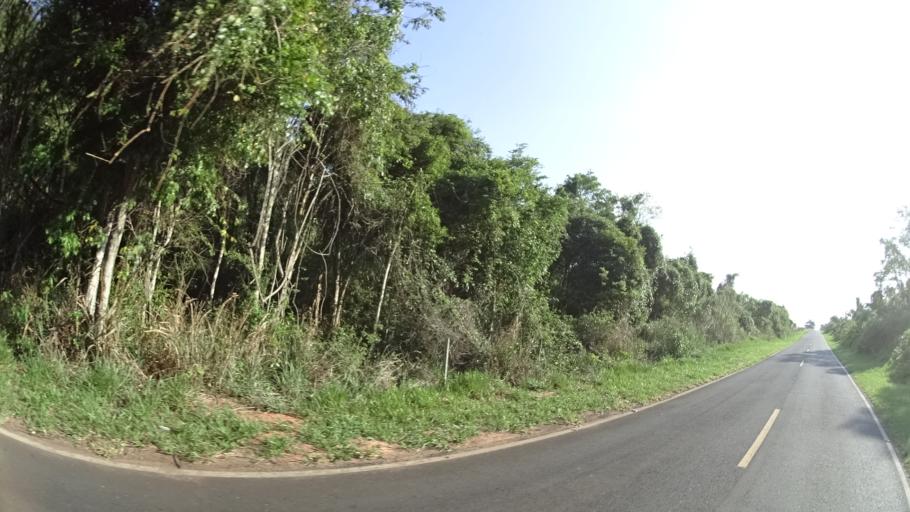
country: BR
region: Sao Paulo
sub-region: Urupes
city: Urupes
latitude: -21.3802
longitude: -49.4869
